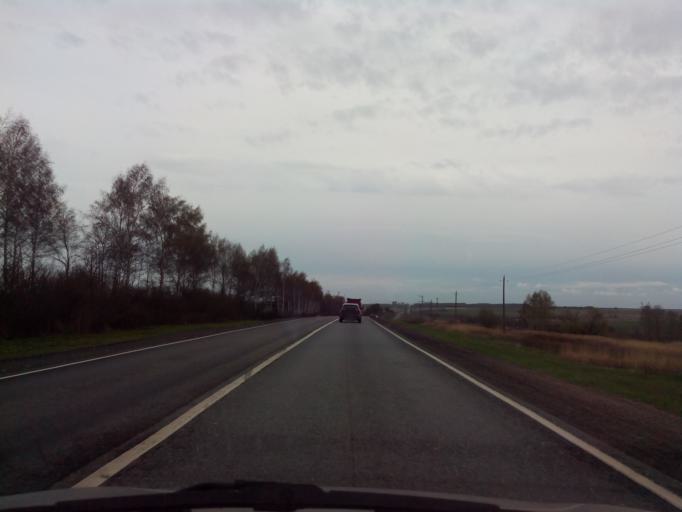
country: RU
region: Moskovskaya
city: Ozherel'ye
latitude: 54.7347
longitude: 38.2574
